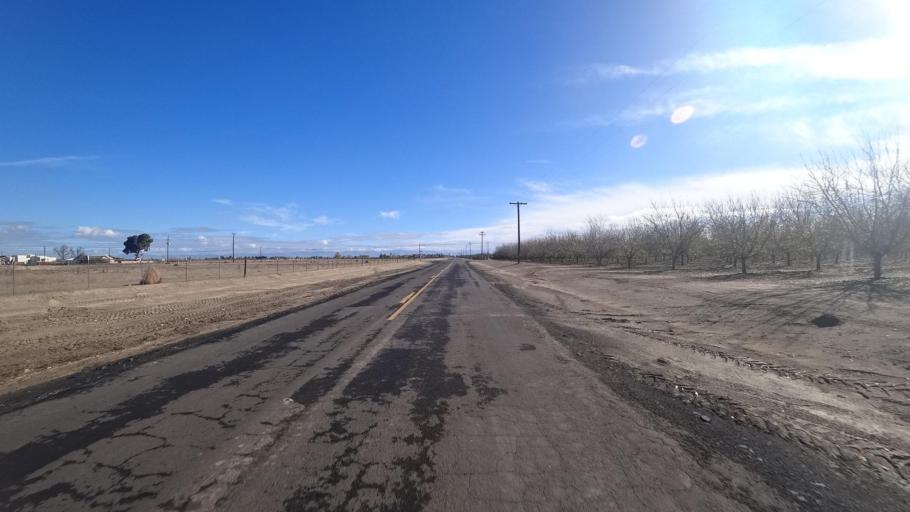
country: US
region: California
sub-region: Kern County
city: Rosedale
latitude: 35.3698
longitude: -119.2356
